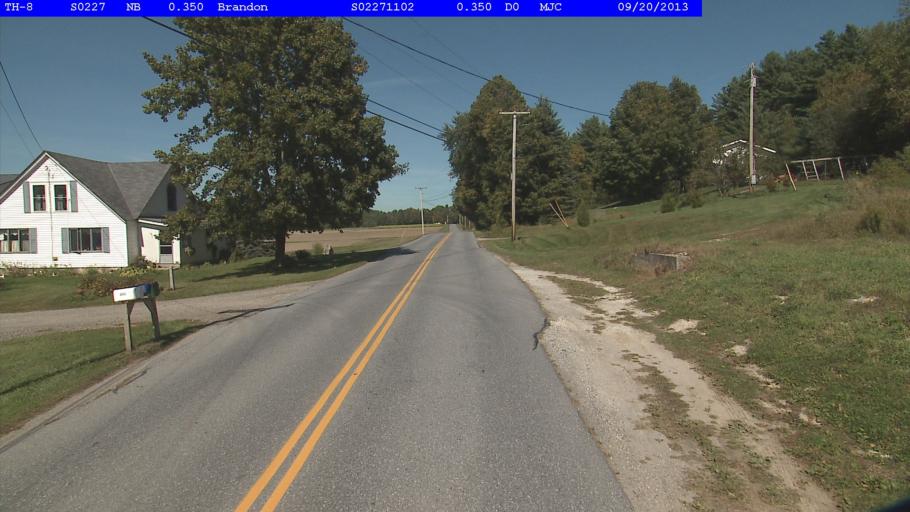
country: US
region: Vermont
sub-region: Rutland County
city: Brandon
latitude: 43.7794
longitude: -73.0524
